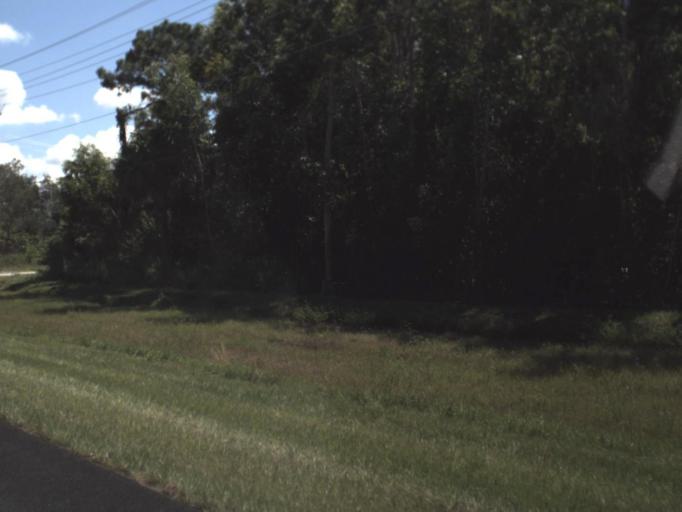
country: US
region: Florida
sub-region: Lee County
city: Pine Island Center
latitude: 26.6373
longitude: -82.0325
